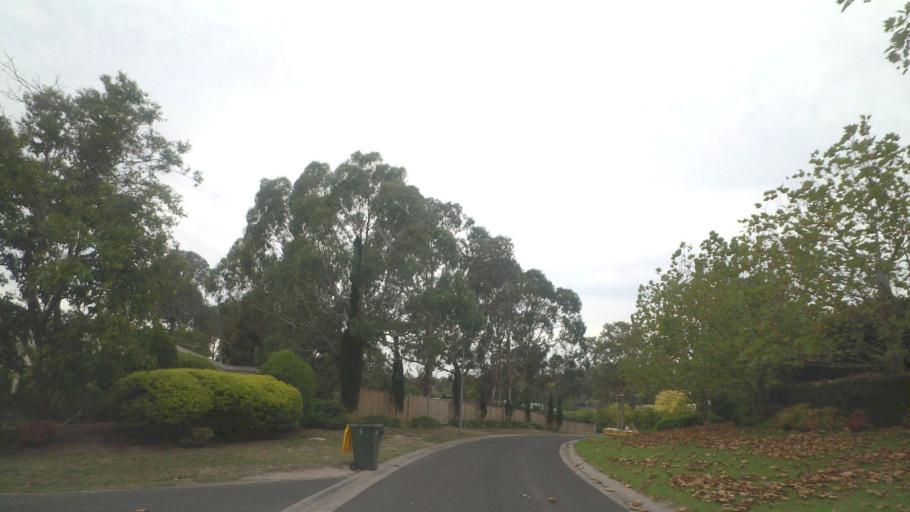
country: AU
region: Victoria
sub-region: Nillumbik
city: North Warrandyte
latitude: -37.7469
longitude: 145.1904
